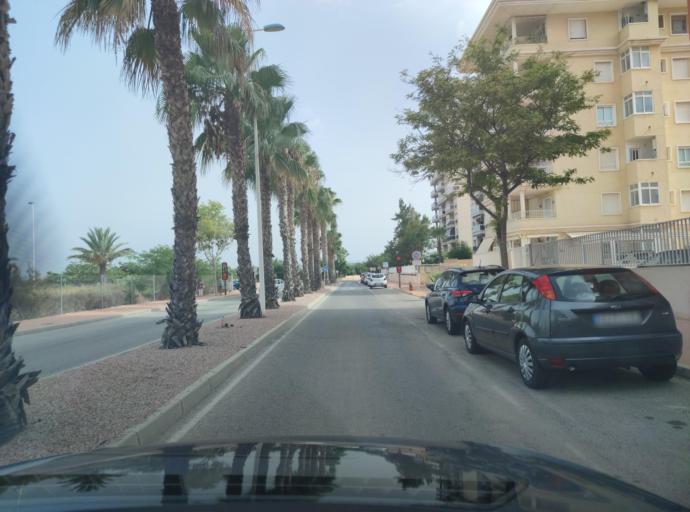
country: ES
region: Valencia
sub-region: Provincia de Alicante
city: Guardamar del Segura
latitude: 38.1021
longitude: -0.6558
